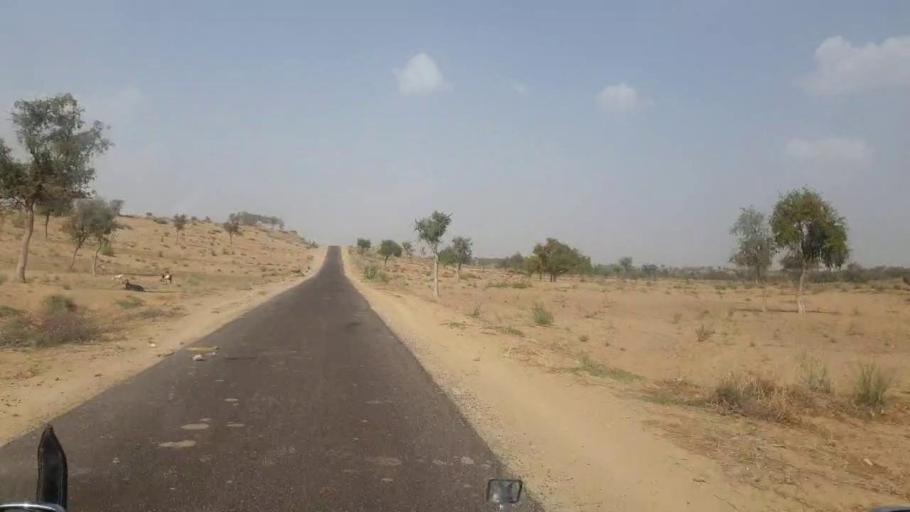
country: PK
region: Sindh
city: Islamkot
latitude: 25.1648
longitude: 70.2871
